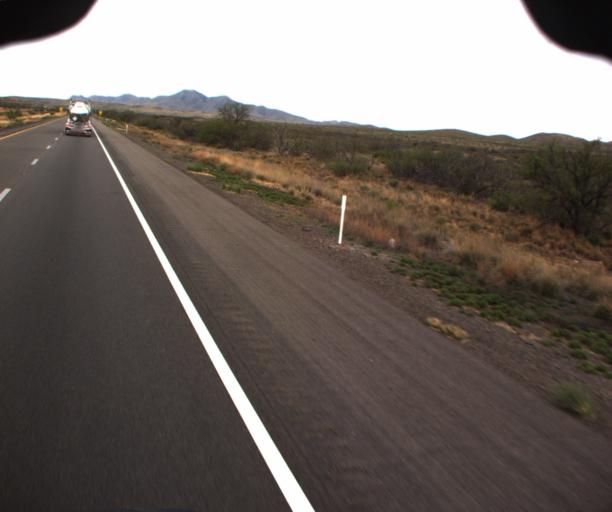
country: US
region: Arizona
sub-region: Cochise County
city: Willcox
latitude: 32.1585
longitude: -109.9799
